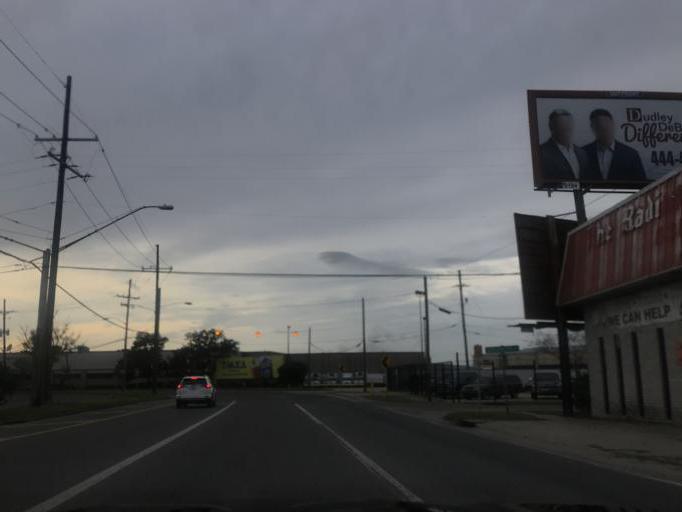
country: US
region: Louisiana
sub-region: Jefferson Parish
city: Jefferson
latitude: 29.9653
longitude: -90.1381
